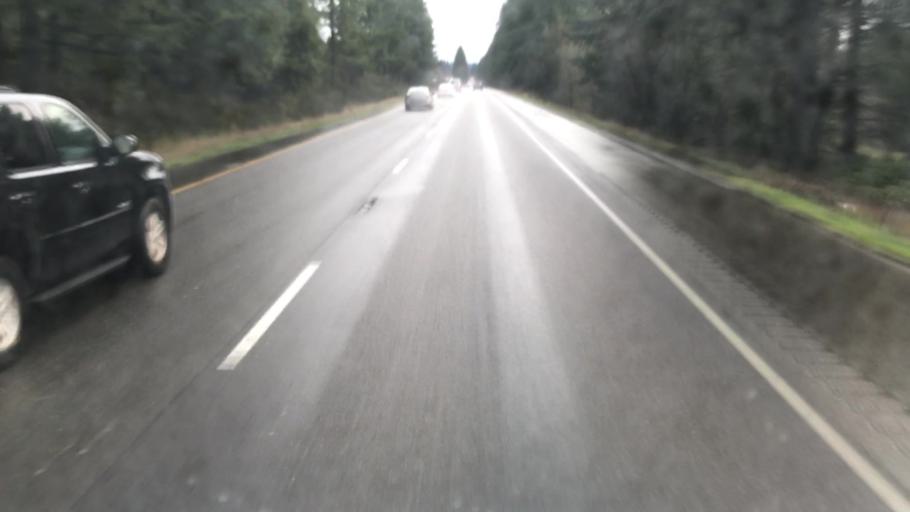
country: US
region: Washington
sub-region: Kitsap County
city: Burley
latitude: 47.4494
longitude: -122.6221
